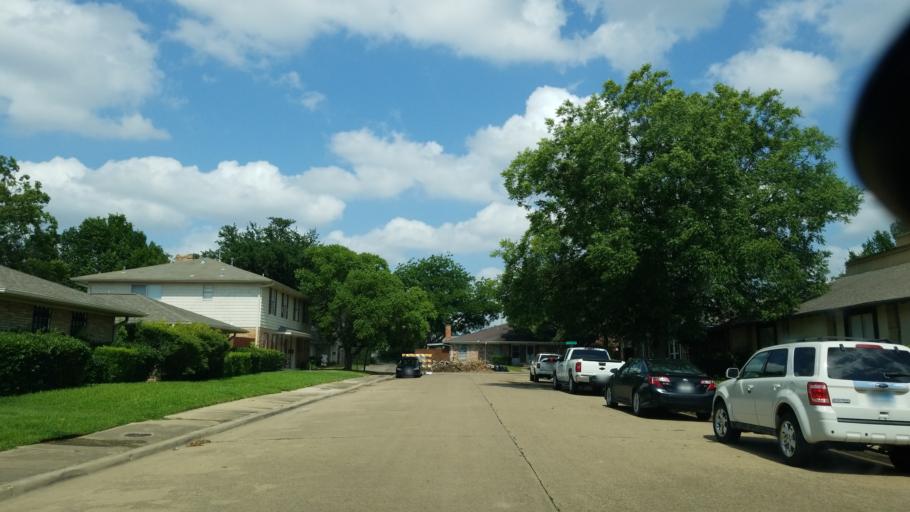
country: US
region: Texas
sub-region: Dallas County
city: Farmers Branch
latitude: 32.8821
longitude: -96.8589
